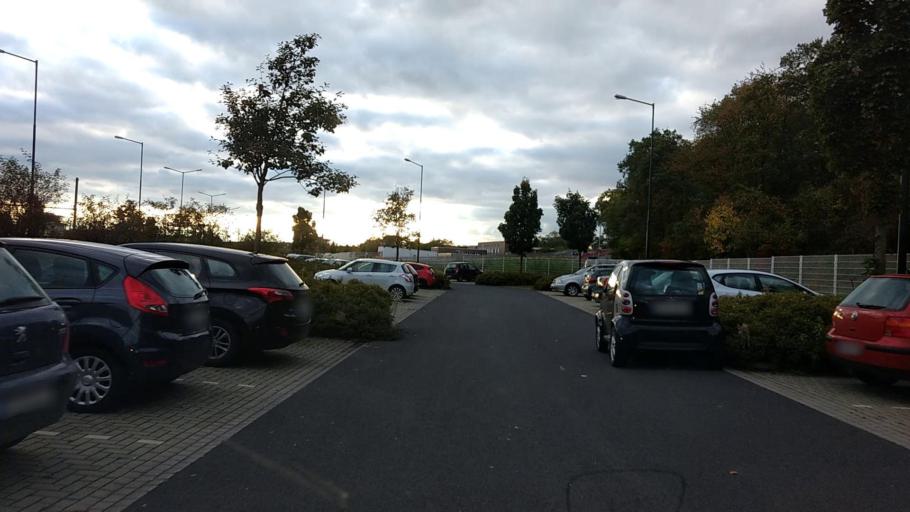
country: DE
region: North Rhine-Westphalia
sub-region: Regierungsbezirk Koln
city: Kerpen
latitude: 50.9188
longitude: 6.7187
